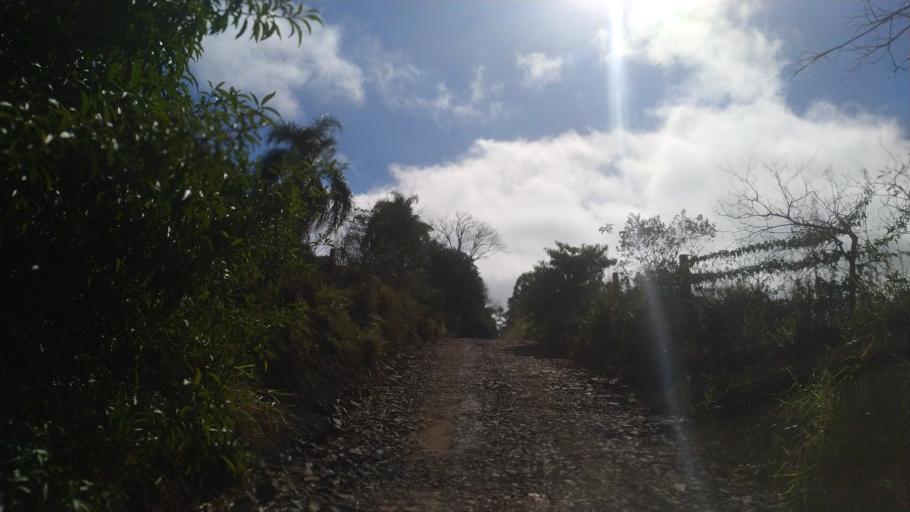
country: BR
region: Santa Catarina
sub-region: Chapeco
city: Chapeco
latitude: -27.1622
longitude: -52.5973
